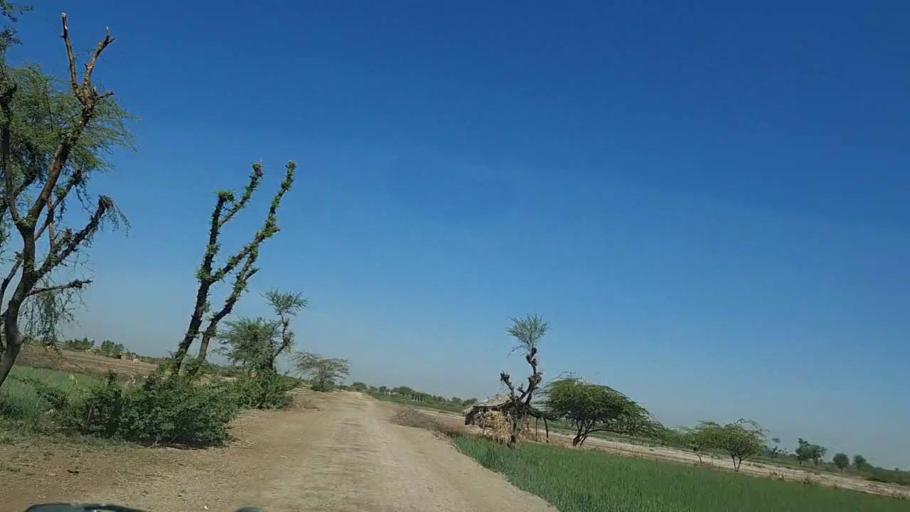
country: PK
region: Sindh
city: Dhoro Naro
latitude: 25.5014
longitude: 69.5115
